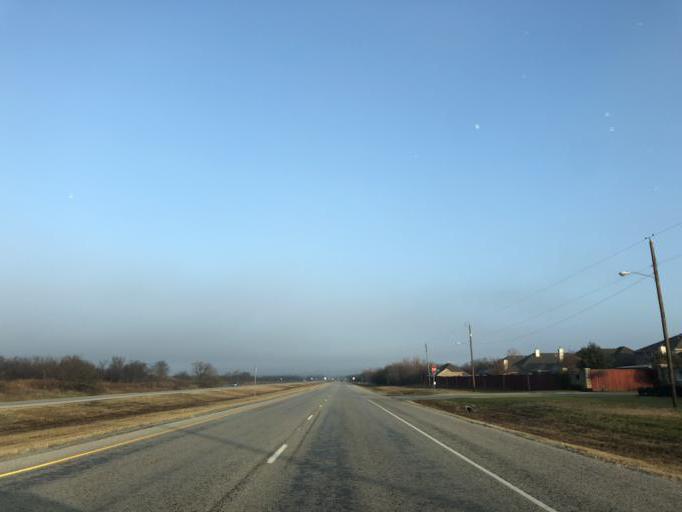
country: US
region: Texas
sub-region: Dallas County
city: Cedar Hill
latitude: 32.6482
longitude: -96.9757
